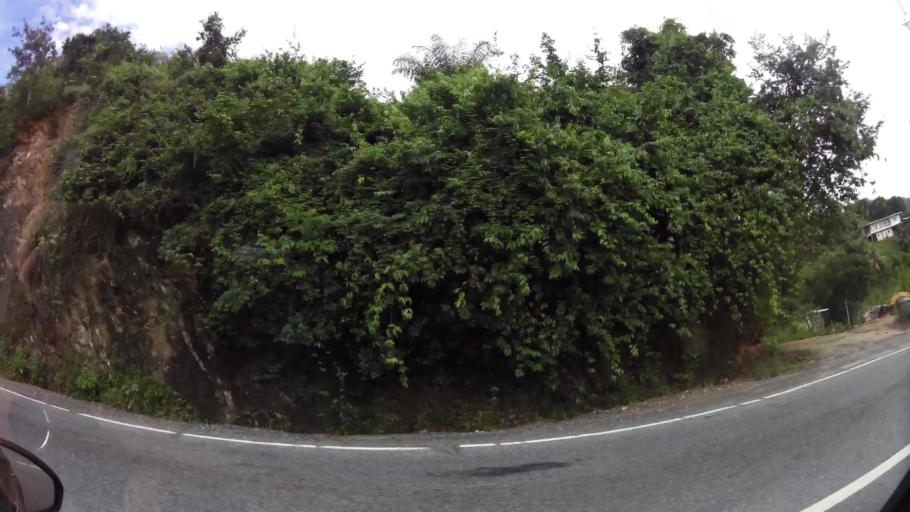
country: TT
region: City of Port of Spain
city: Port-of-Spain
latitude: 10.6736
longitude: -61.5030
